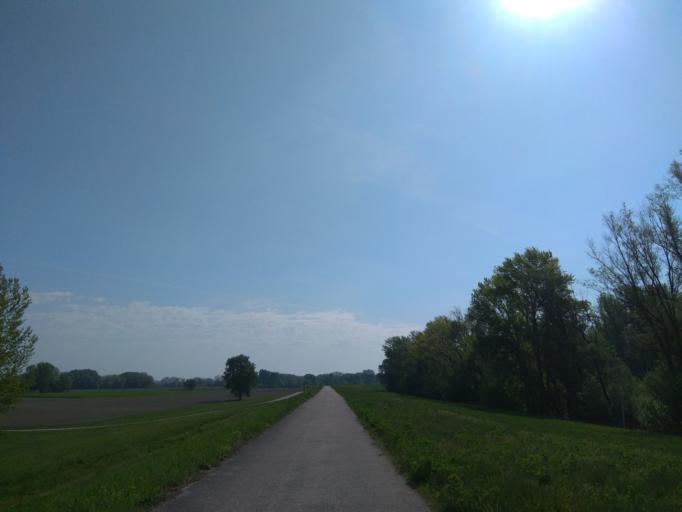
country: SK
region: Trnavsky
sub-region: Okres Dunajska Streda
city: Velky Meder
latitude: 47.7961
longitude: 17.6754
